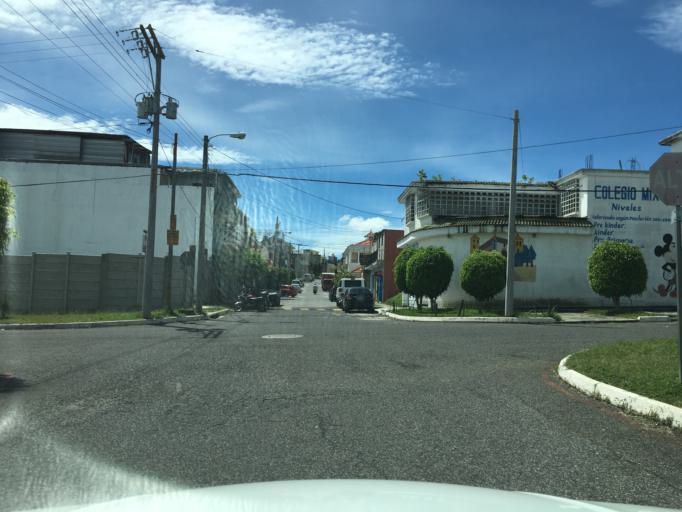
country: GT
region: Guatemala
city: Mixco
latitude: 14.6575
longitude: -90.5656
